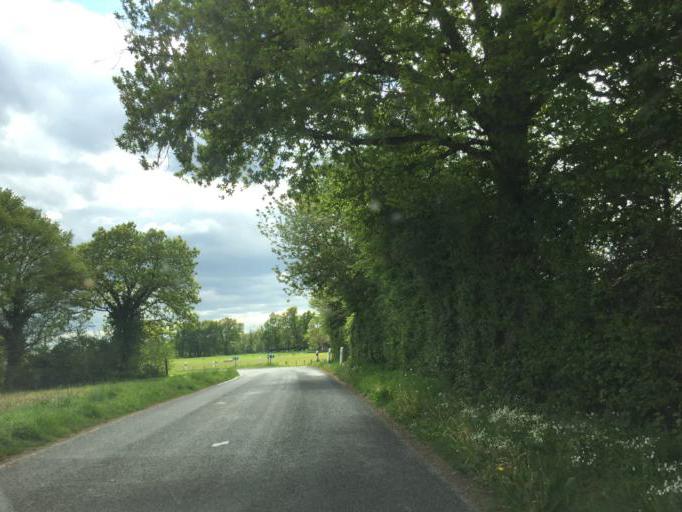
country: FR
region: Rhone-Alpes
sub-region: Departement de l'Ain
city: Amberieux-en-Dombes
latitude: 46.0171
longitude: 4.9228
